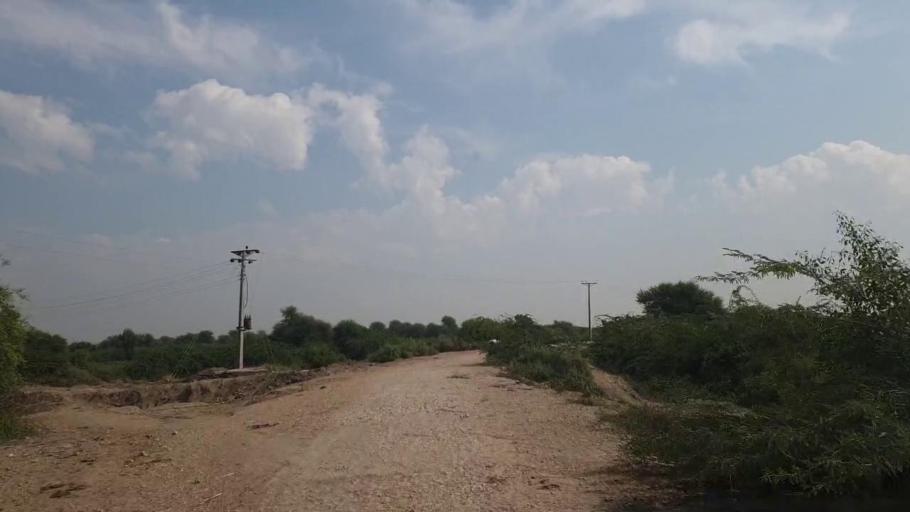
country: PK
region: Sindh
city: Tando Bago
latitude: 24.9327
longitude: 69.0051
